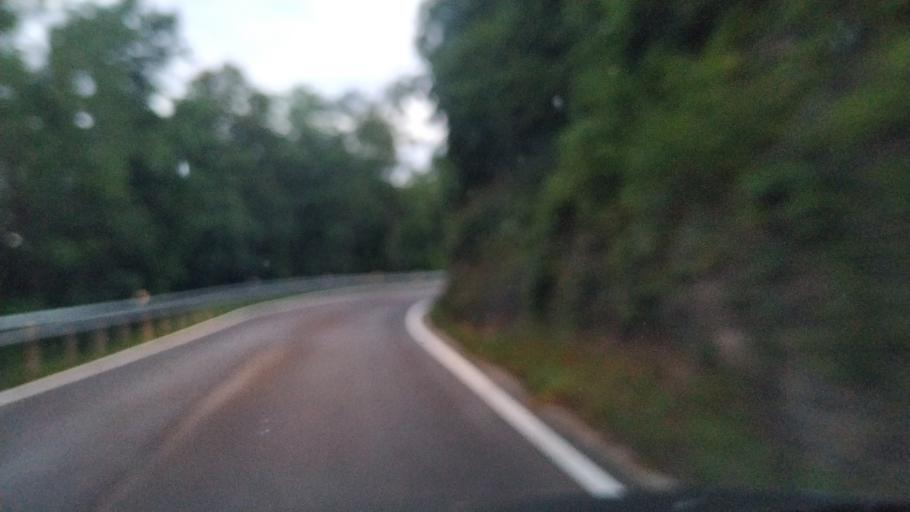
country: IT
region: Trentino-Alto Adige
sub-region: Provincia di Trento
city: Castelfondo
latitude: 46.4430
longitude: 11.1177
